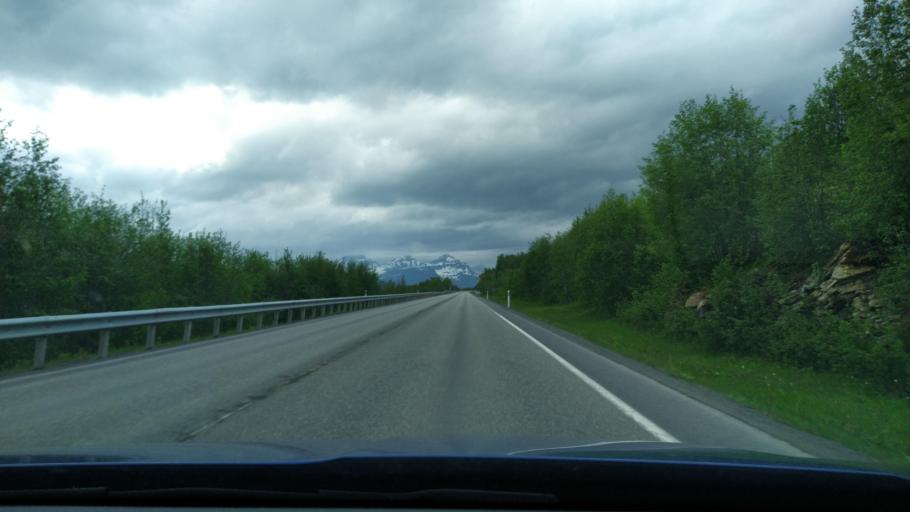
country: NO
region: Troms
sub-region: Balsfjord
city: Storsteinnes
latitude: 69.2535
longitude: 19.4358
